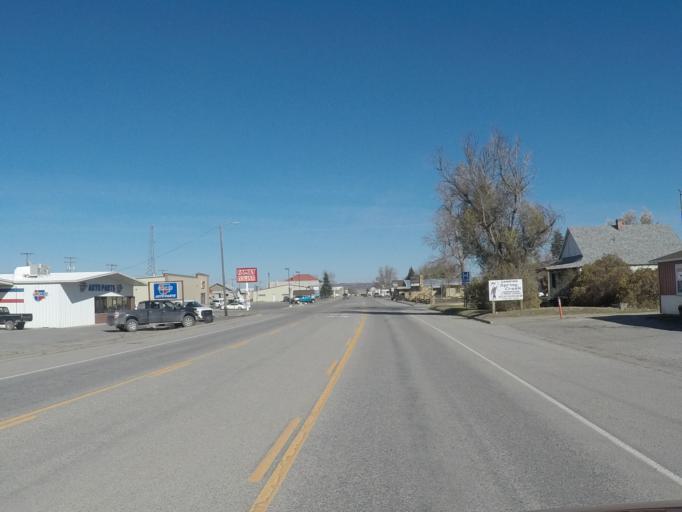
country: US
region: Montana
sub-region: Sweet Grass County
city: Big Timber
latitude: 45.8324
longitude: -109.9595
